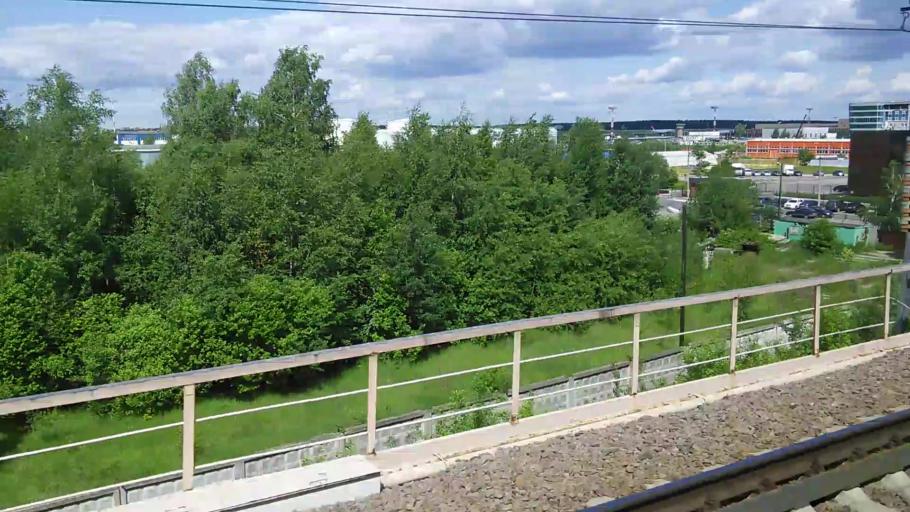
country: RU
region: Moskovskaya
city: Sheremet'yevskiy
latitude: 55.9651
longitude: 37.4269
